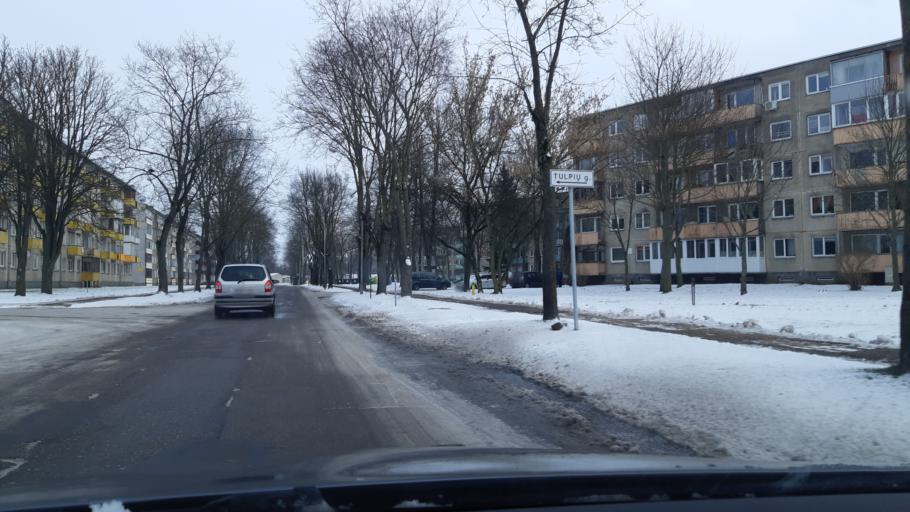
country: LT
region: Kauno apskritis
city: Kedainiai
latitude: 55.2908
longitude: 23.9847
